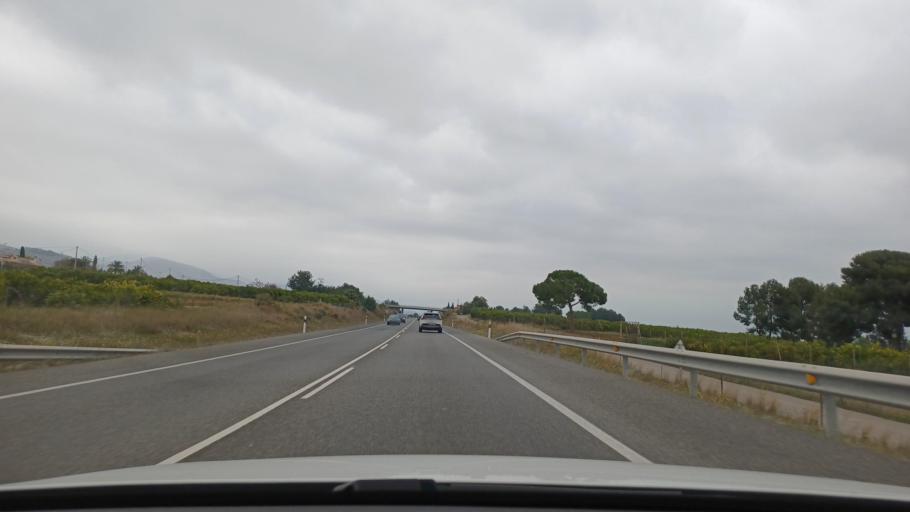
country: ES
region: Valencia
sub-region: Provincia de Castello
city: Castello de la Plana
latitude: 40.0053
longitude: -0.0605
